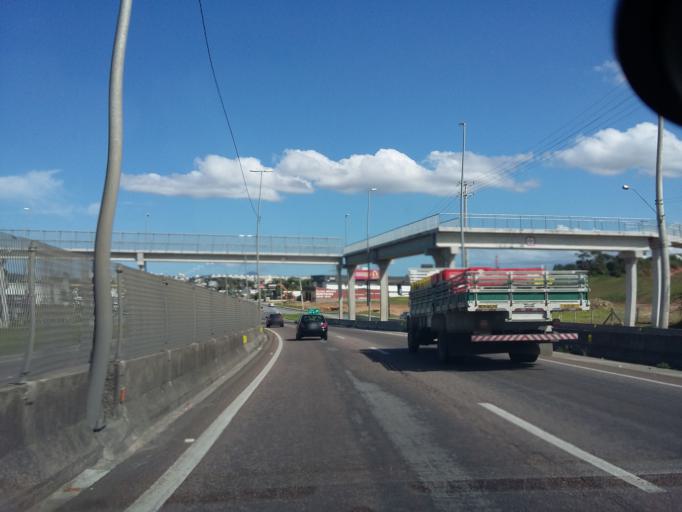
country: BR
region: Santa Catarina
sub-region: Biguacu
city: Biguacu
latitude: -27.5229
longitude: -48.6371
